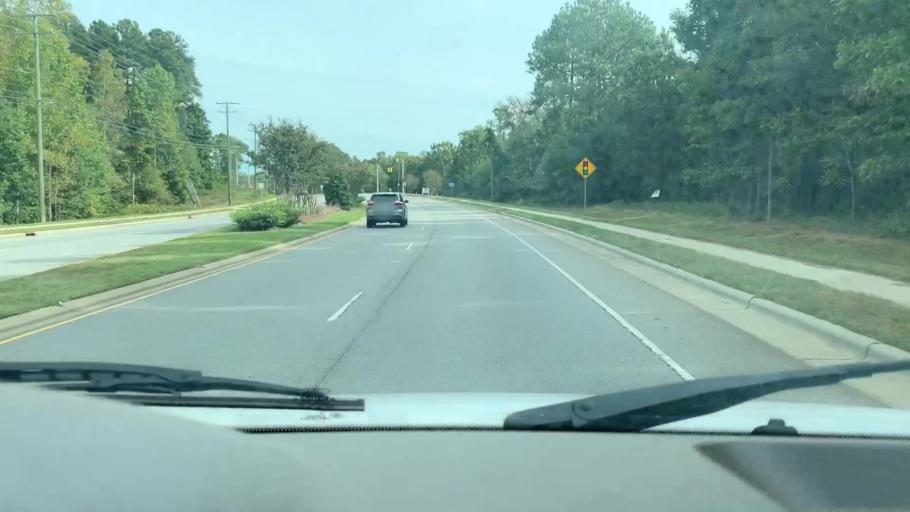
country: US
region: North Carolina
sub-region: Catawba County
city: Lake Norman of Catawba
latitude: 35.5644
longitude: -80.9113
